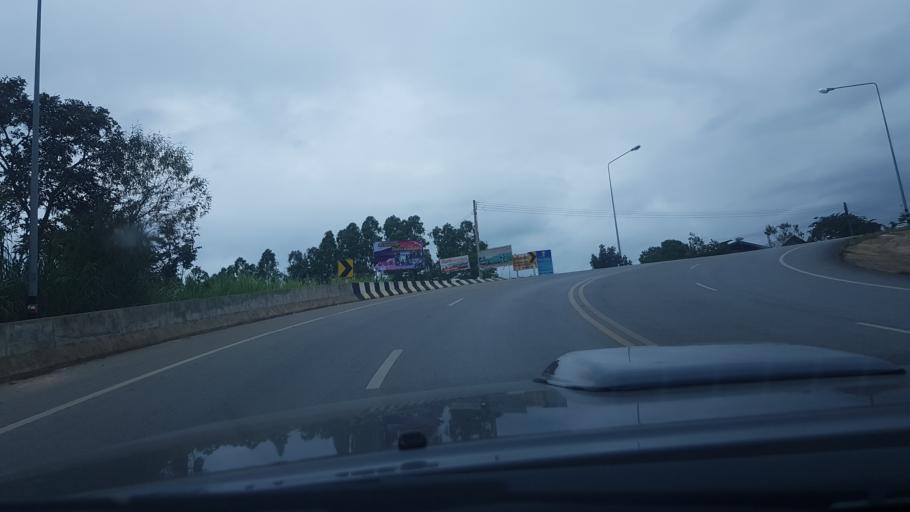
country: TH
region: Phetchabun
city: Khao Kho
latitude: 16.5690
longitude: 100.9932
